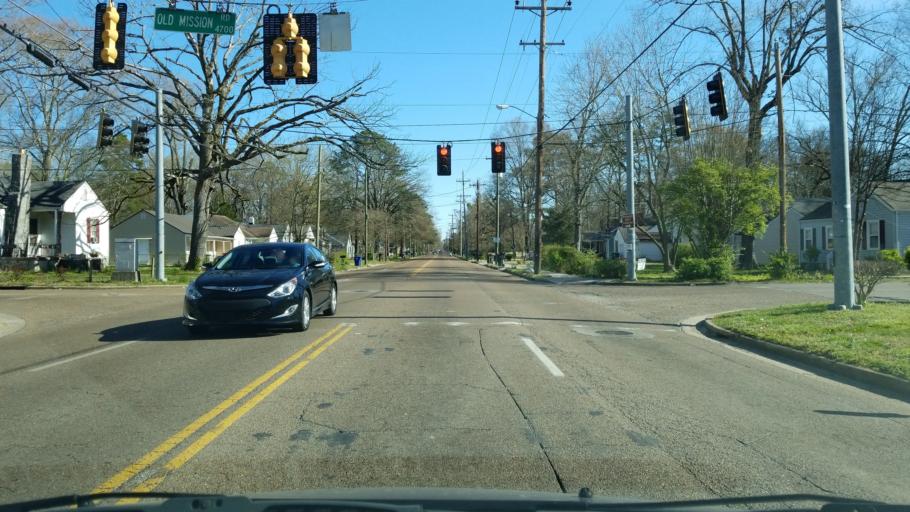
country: US
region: Tennessee
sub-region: Hamilton County
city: East Ridge
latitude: 35.0165
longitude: -85.2263
